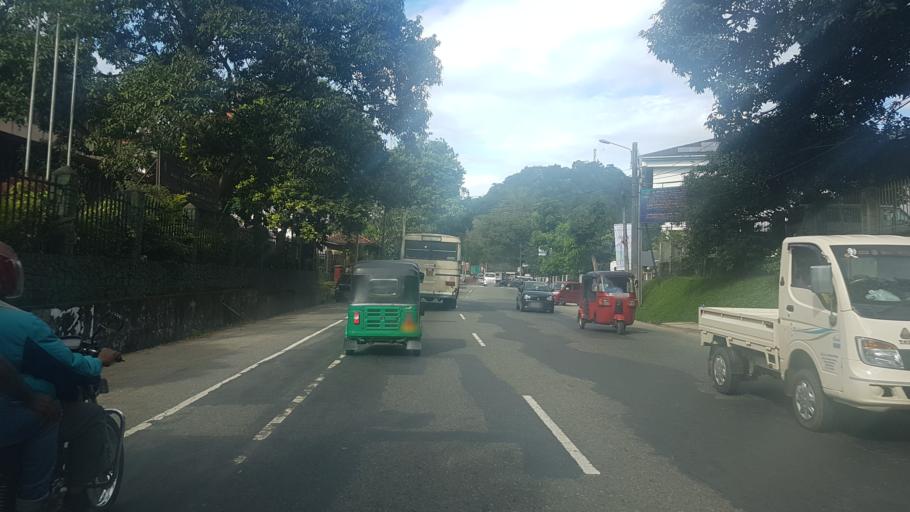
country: LK
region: Central
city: Kandy
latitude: 7.2692
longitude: 80.6045
